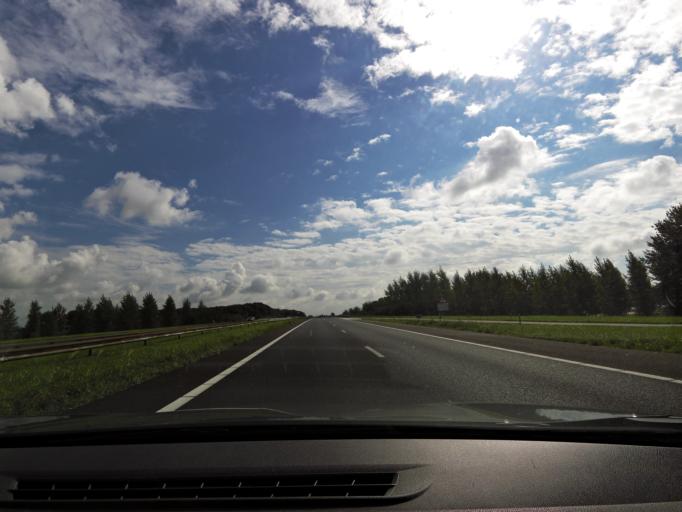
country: NL
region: Zeeland
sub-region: Gemeente Goes
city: Goes
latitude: 51.4764
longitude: 3.9347
